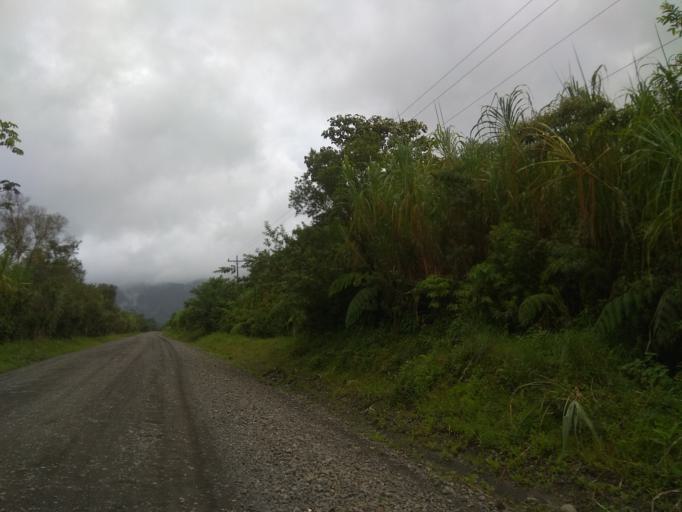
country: CR
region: Alajuela
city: La Fortuna
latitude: 10.4578
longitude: -84.7390
